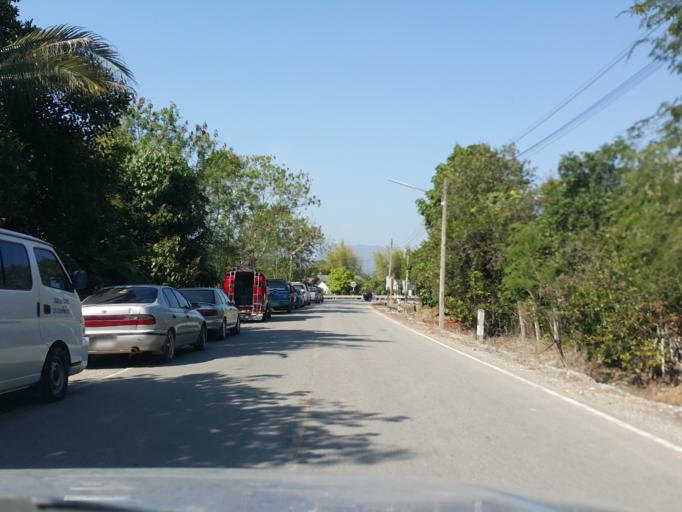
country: TH
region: Chiang Mai
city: Mae Wang
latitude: 18.5765
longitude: 98.7938
